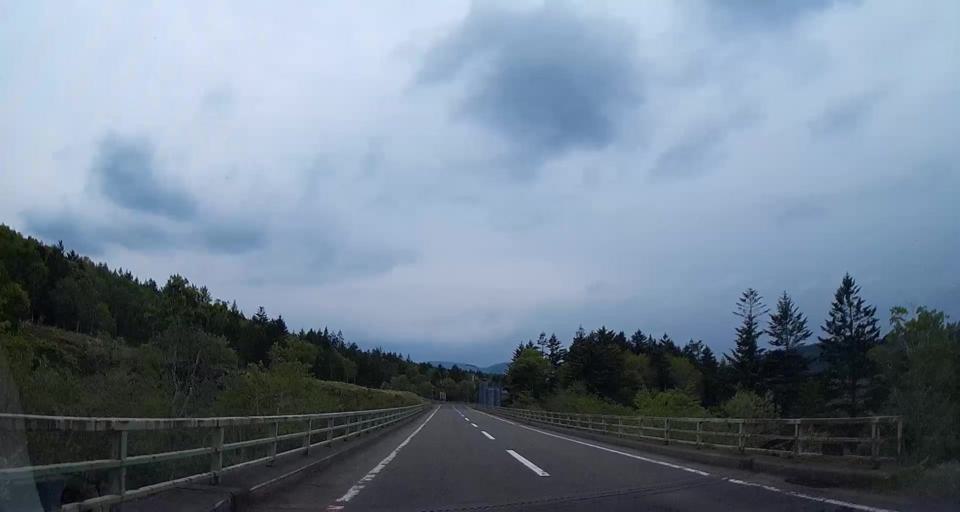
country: JP
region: Hokkaido
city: Shiraoi
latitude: 42.6727
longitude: 141.1595
